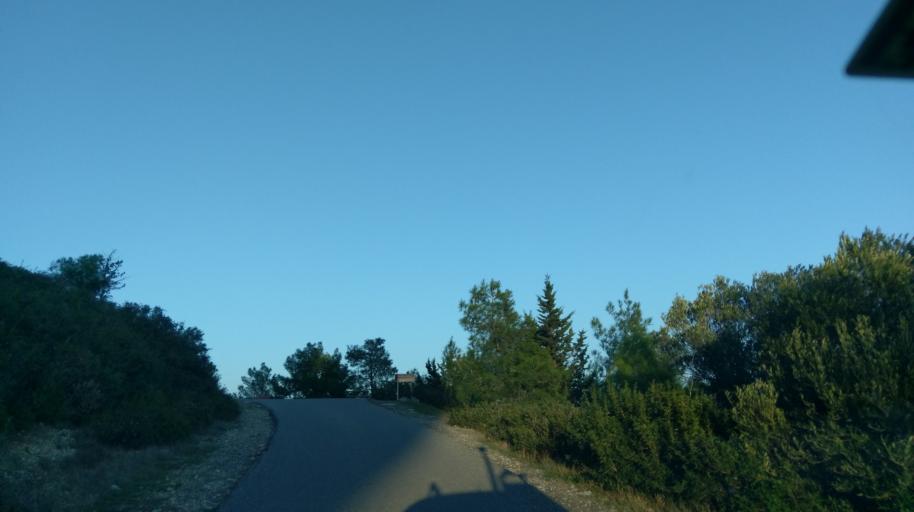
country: CY
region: Ammochostos
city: Trikomo
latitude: 35.4058
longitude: 33.9234
